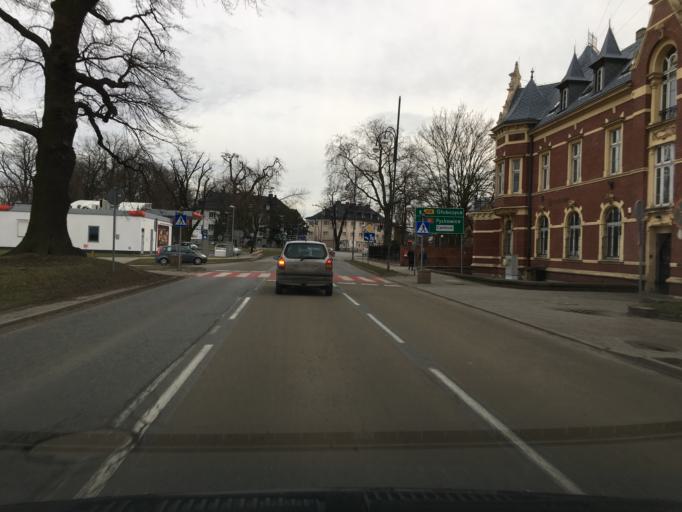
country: PL
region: Opole Voivodeship
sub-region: Powiat kedzierzynsko-kozielski
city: Kozle
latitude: 50.3362
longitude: 18.1462
